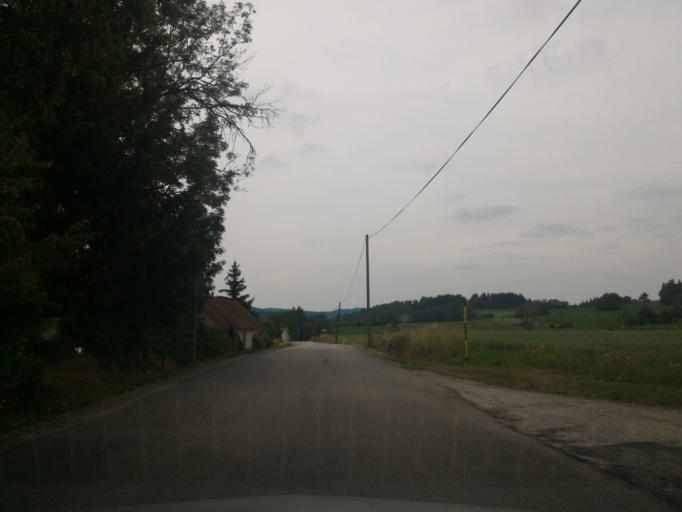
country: CZ
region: Vysocina
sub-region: Okres Jihlava
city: Telc
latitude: 49.2073
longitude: 15.3890
